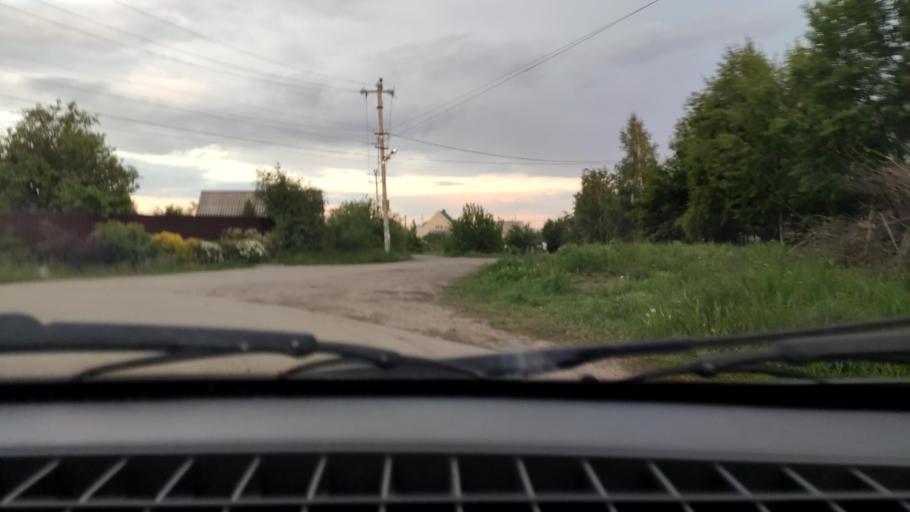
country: RU
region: Voronezj
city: Somovo
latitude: 51.6797
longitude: 39.3260
